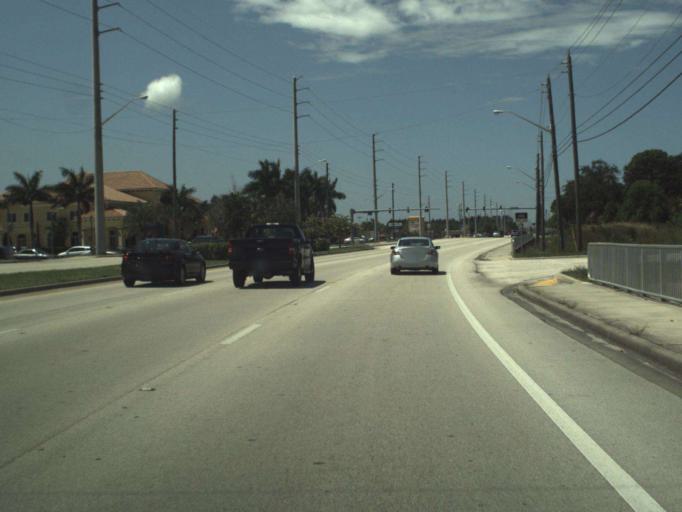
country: US
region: Florida
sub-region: Saint Lucie County
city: River Park
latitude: 27.3358
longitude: -80.3257
